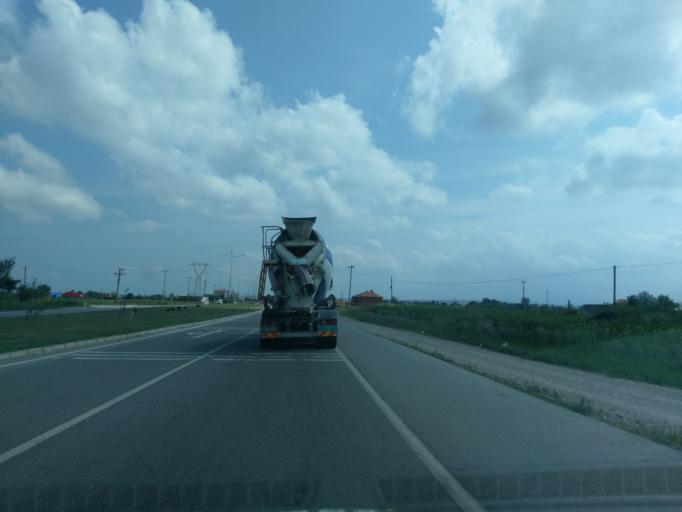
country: TR
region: Samsun
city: Bafra
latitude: 41.5783
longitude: 35.8504
